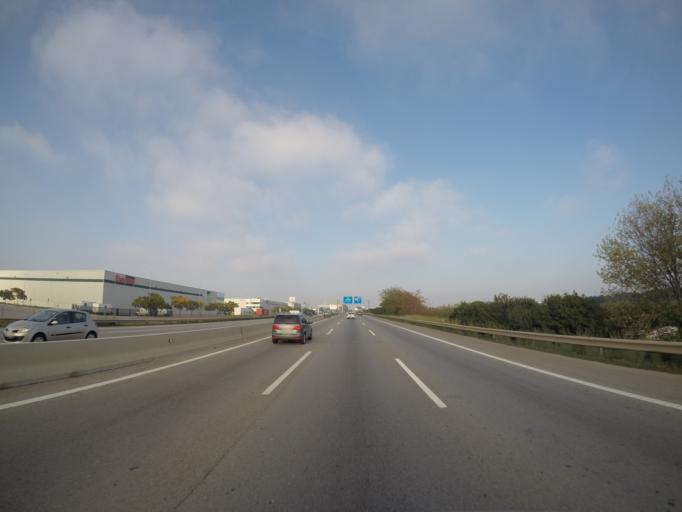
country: ES
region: Catalonia
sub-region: Provincia de Barcelona
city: Sant Boi de Llobregat
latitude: 41.3229
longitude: 2.0432
